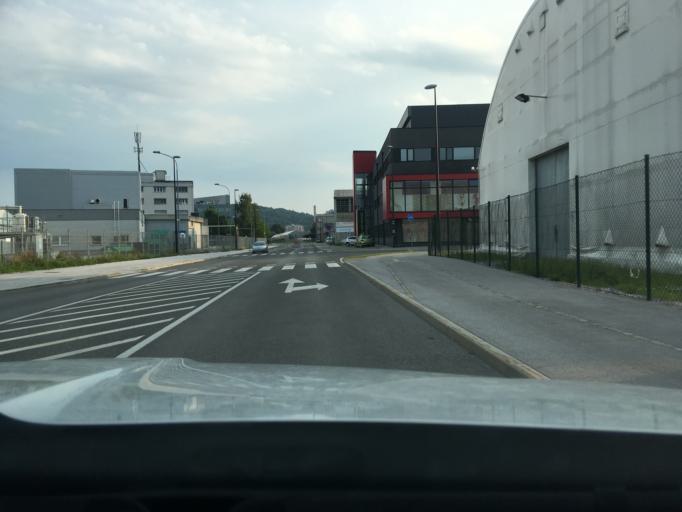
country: SI
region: Ljubljana
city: Ljubljana
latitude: 46.0801
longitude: 14.4984
